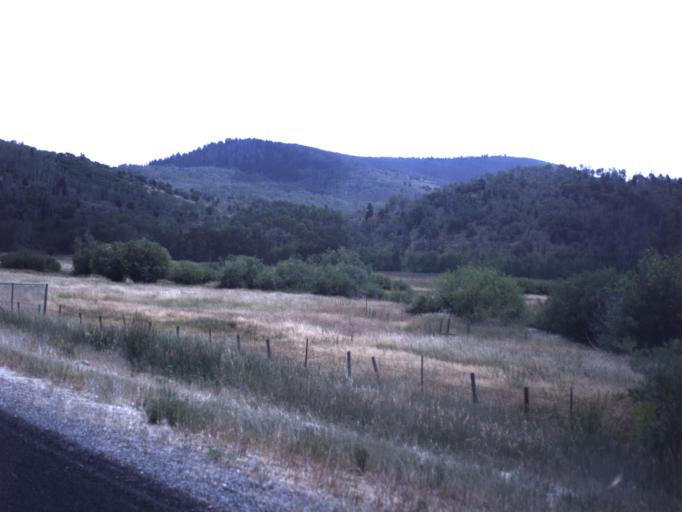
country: US
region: Utah
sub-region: Summit County
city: Francis
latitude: 40.5575
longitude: -111.1350
